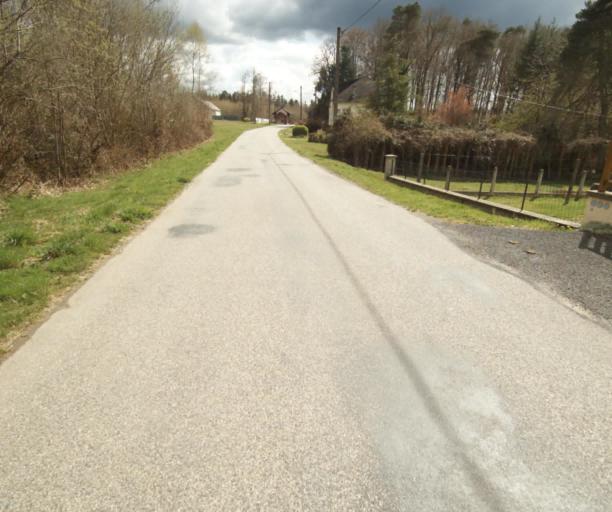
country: FR
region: Limousin
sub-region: Departement de la Correze
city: Correze
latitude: 45.2694
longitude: 1.9776
